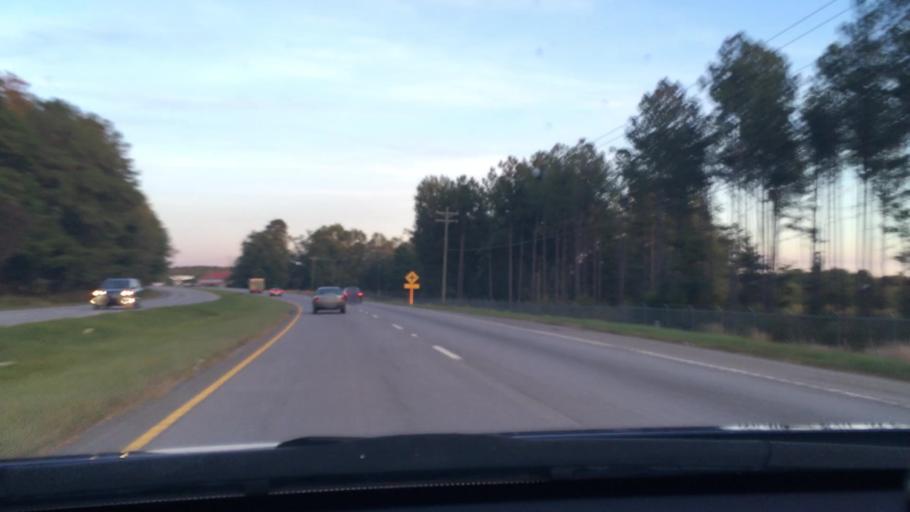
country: US
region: South Carolina
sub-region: Richland County
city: Hopkins
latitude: 33.9390
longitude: -80.7911
